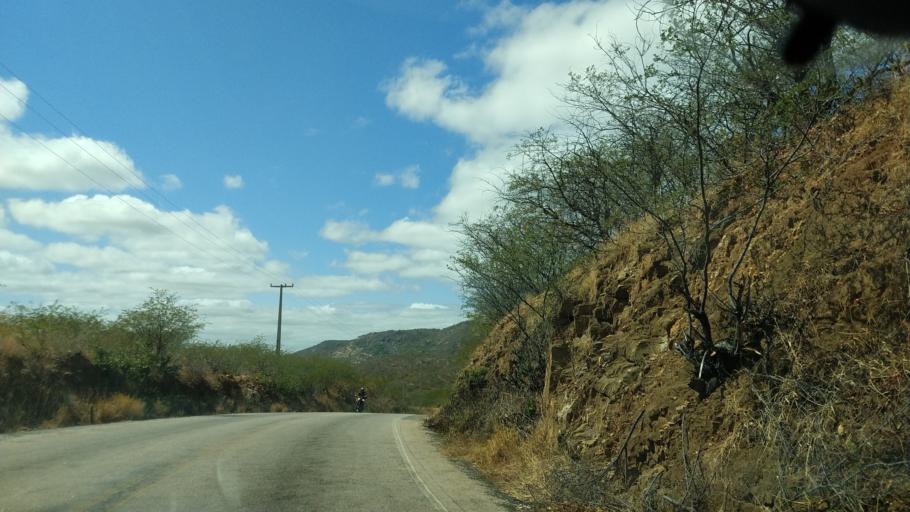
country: BR
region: Rio Grande do Norte
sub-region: Currais Novos
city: Currais Novos
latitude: -6.2626
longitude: -36.5962
